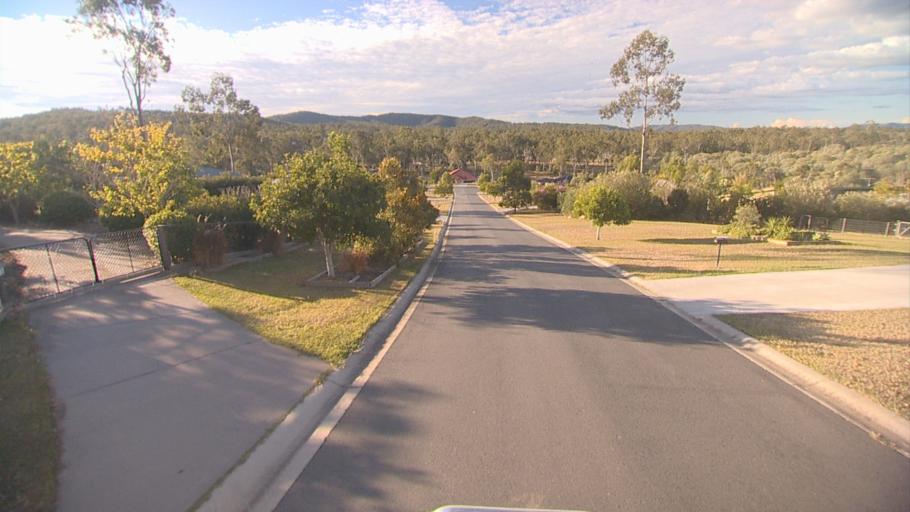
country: AU
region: Queensland
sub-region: Logan
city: Cedar Vale
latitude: -27.8650
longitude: 153.0836
